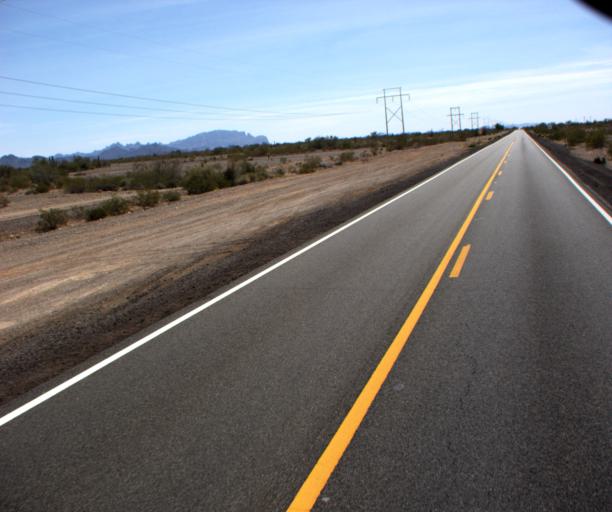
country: US
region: Arizona
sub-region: La Paz County
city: Quartzsite
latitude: 33.5776
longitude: -114.2171
